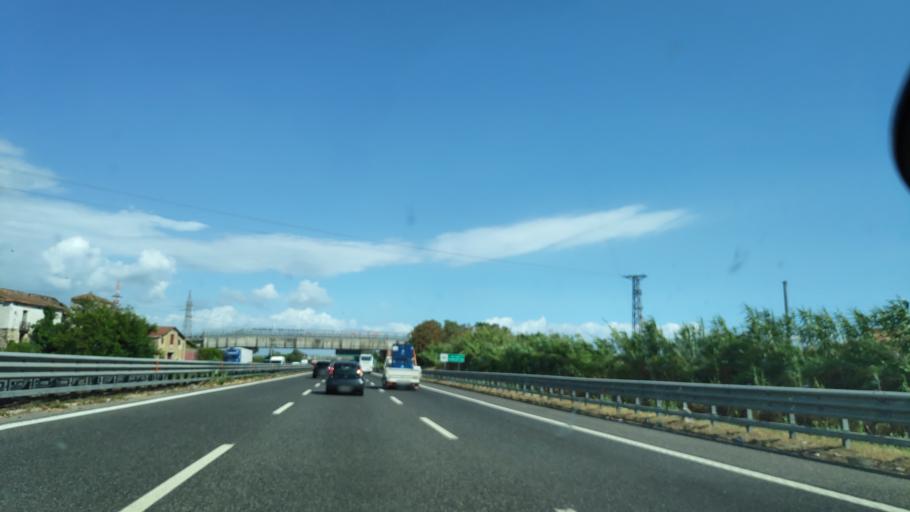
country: IT
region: Campania
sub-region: Provincia di Salerno
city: Sant'Antonio
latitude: 40.6379
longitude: 14.9026
